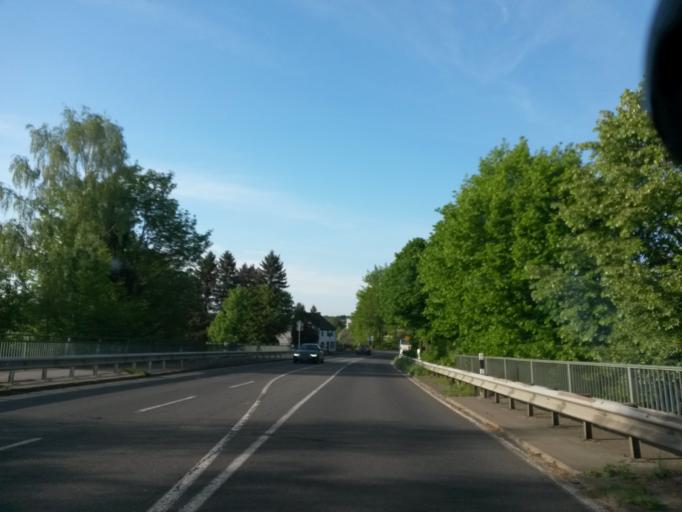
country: DE
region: North Rhine-Westphalia
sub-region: Regierungsbezirk Koln
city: Much
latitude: 50.8802
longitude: 7.3377
